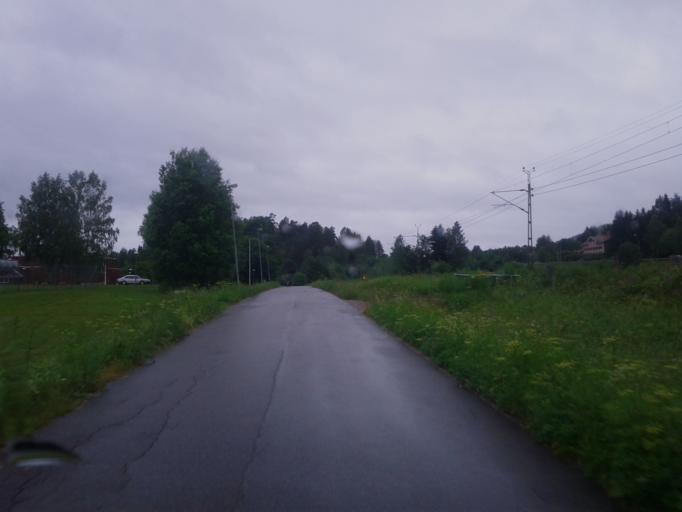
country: SE
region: Vaesternorrland
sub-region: Ange Kommun
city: Fransta
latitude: 62.4170
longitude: 16.5735
